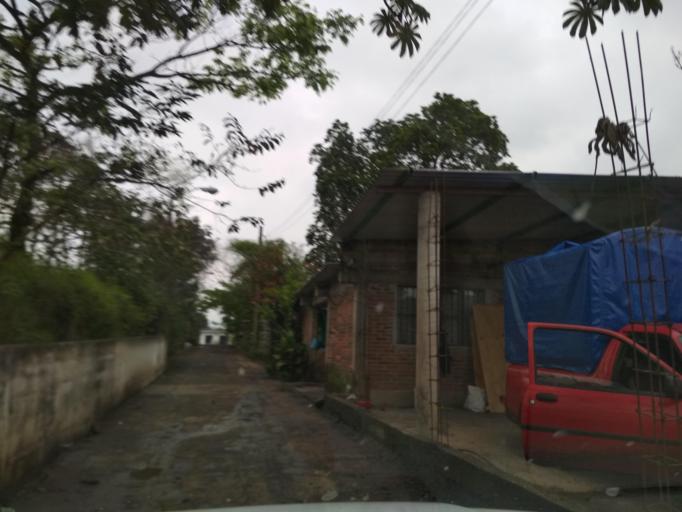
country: MX
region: Veracruz
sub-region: Cordoba
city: Veinte de Noviembre
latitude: 18.8682
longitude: -96.9564
